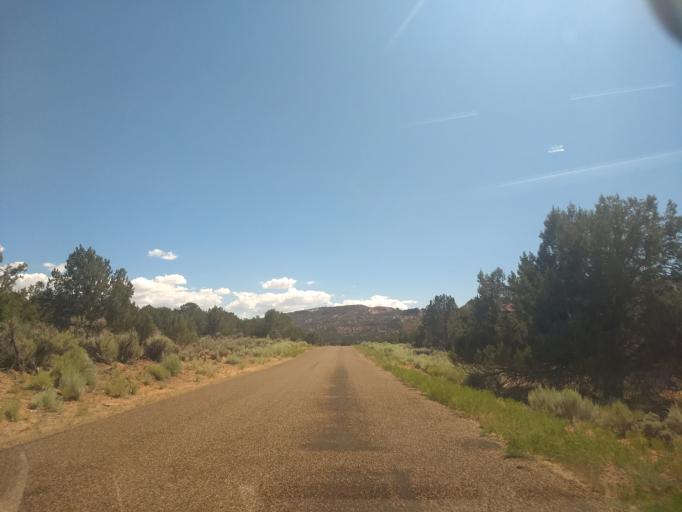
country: US
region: Utah
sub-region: Washington County
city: Hildale
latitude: 37.0031
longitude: -112.8593
